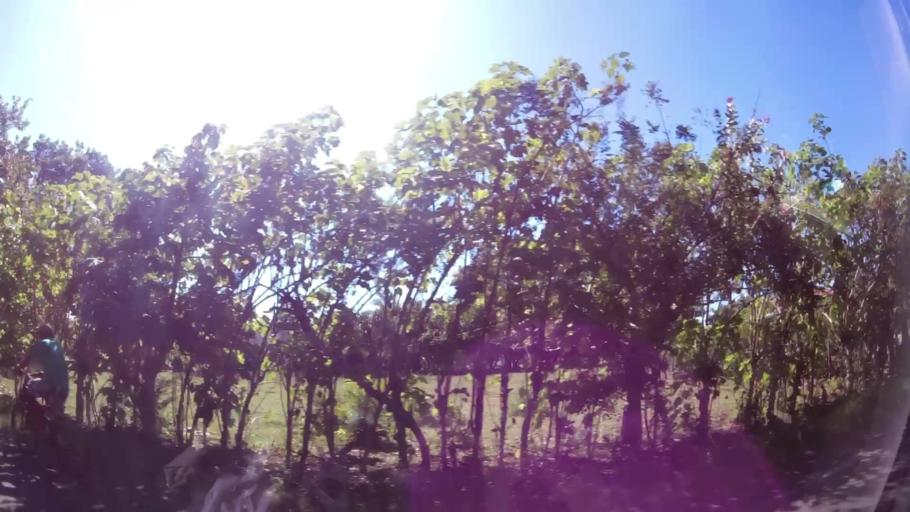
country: GT
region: Escuintla
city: Iztapa
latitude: 13.9233
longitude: -90.5992
